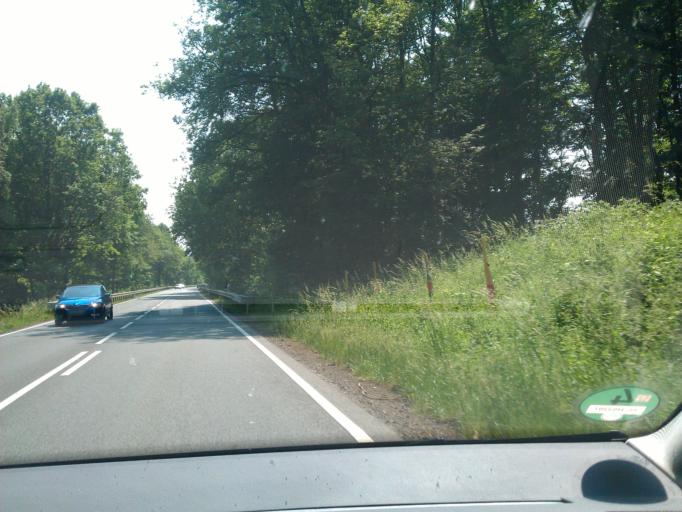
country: DE
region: Hesse
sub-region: Regierungsbezirk Darmstadt
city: Niedernhausen
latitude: 50.1212
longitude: 8.2897
